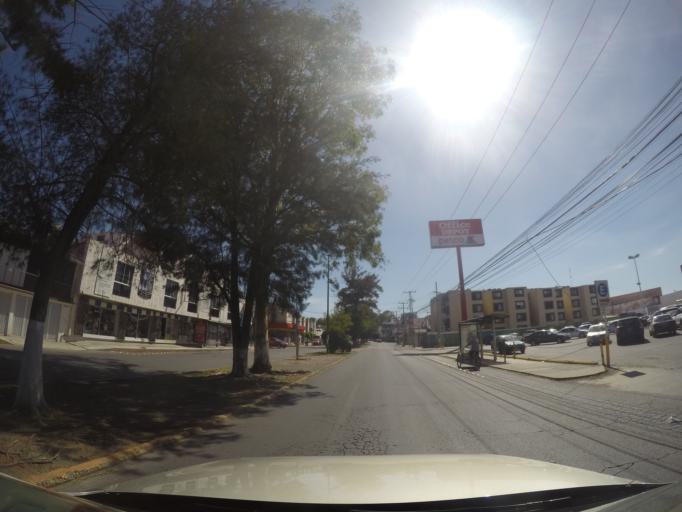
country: MX
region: San Luis Potosi
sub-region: San Luis Potosi
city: San Luis Potosi
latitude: 22.1519
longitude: -101.0119
